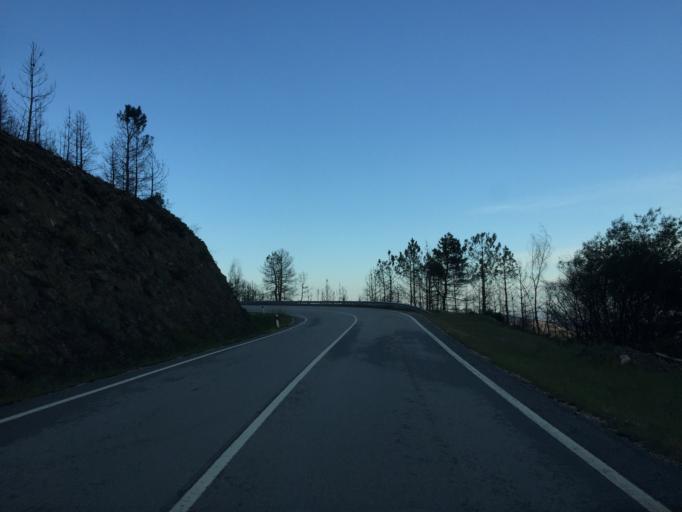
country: PT
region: Coimbra
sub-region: Gois
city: Gois
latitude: 40.1001
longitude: -8.0495
